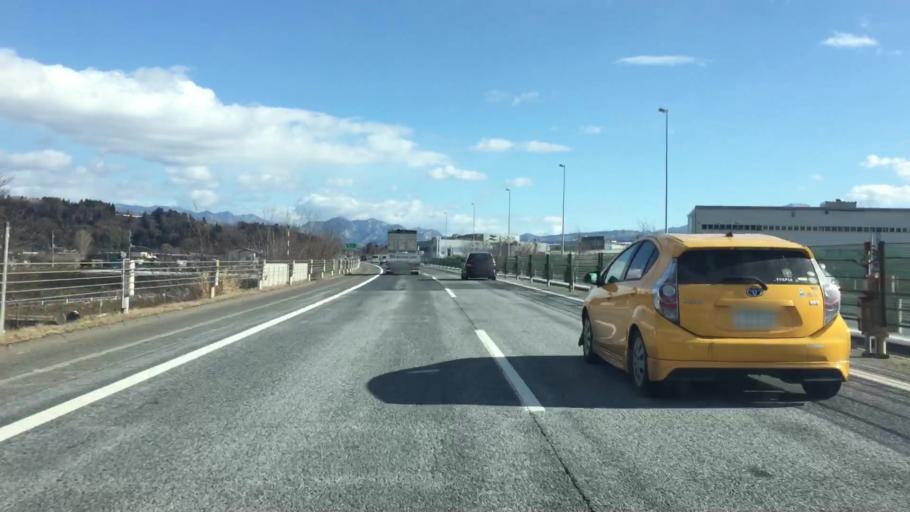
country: JP
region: Gunma
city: Numata
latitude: 36.6705
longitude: 139.0474
